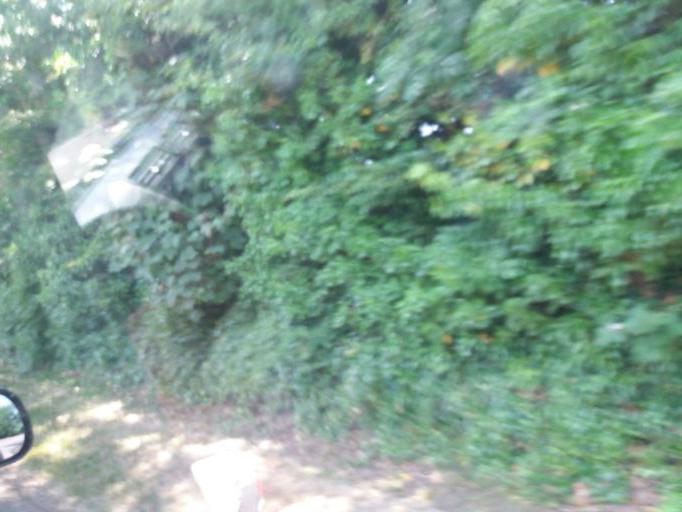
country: IE
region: Leinster
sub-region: An Mhi
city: Slane
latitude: 53.7156
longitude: -6.5379
